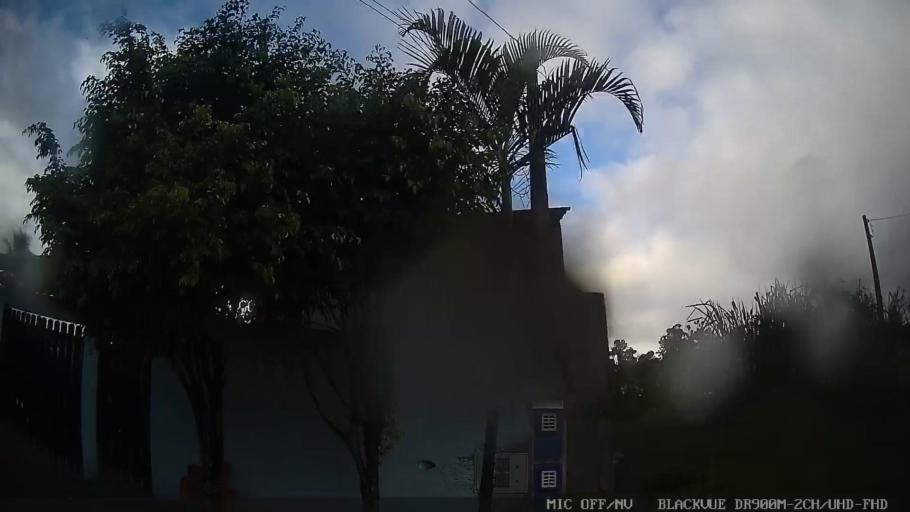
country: BR
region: Sao Paulo
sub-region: Peruibe
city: Peruibe
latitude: -24.2300
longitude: -46.9088
